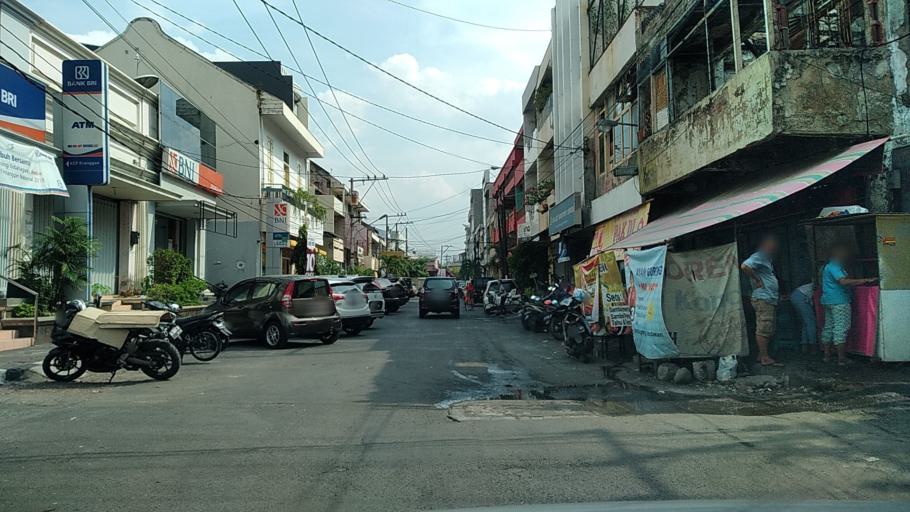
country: ID
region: Central Java
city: Semarang
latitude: -6.9754
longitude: 110.4282
